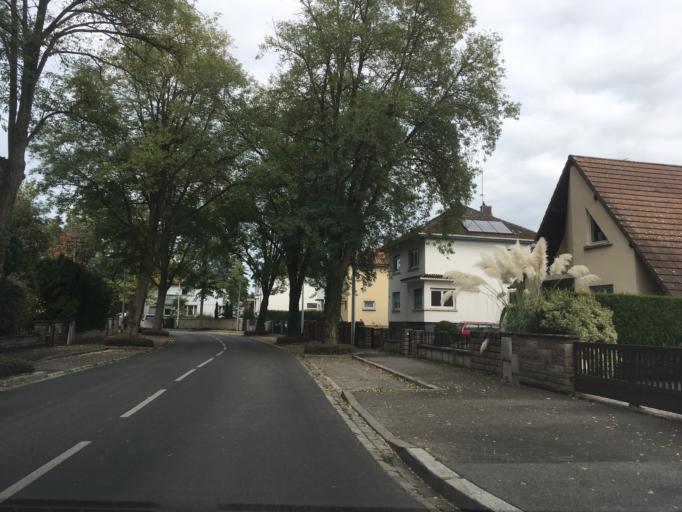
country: FR
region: Alsace
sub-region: Departement du Bas-Rhin
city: Illkirch-Graffenstaden
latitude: 48.5303
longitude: 7.7609
